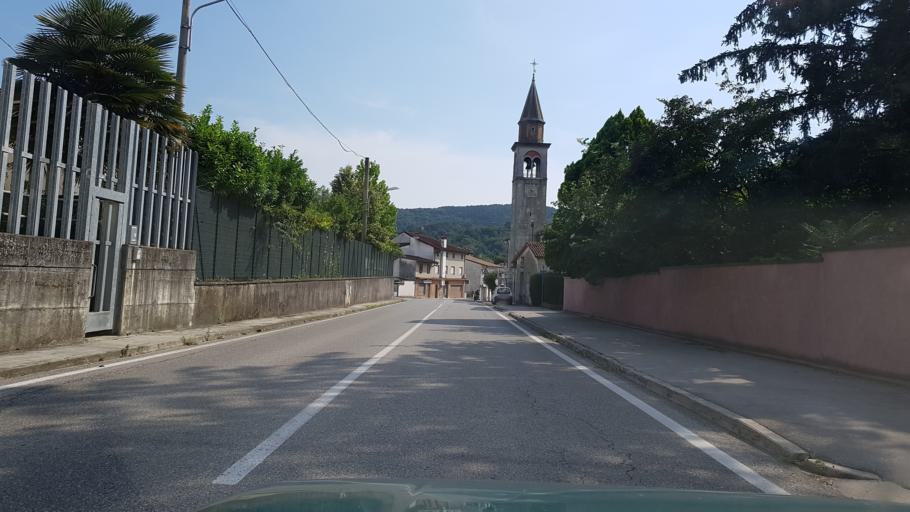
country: IT
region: Friuli Venezia Giulia
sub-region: Provincia di Gorizia
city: Savogna d'Isonzo
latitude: 45.9034
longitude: 13.5726
